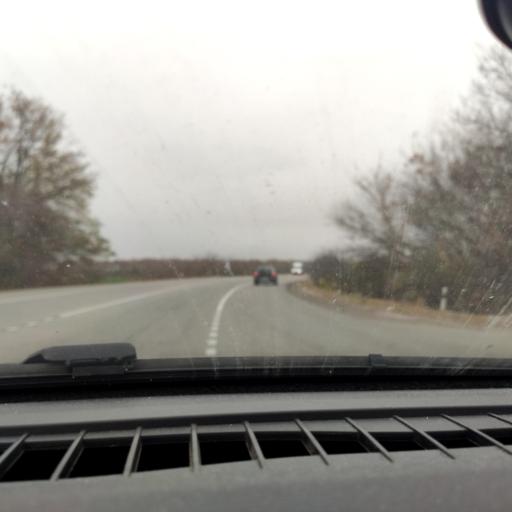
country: RU
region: Voronezj
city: Devitsa
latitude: 51.6033
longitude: 38.9714
